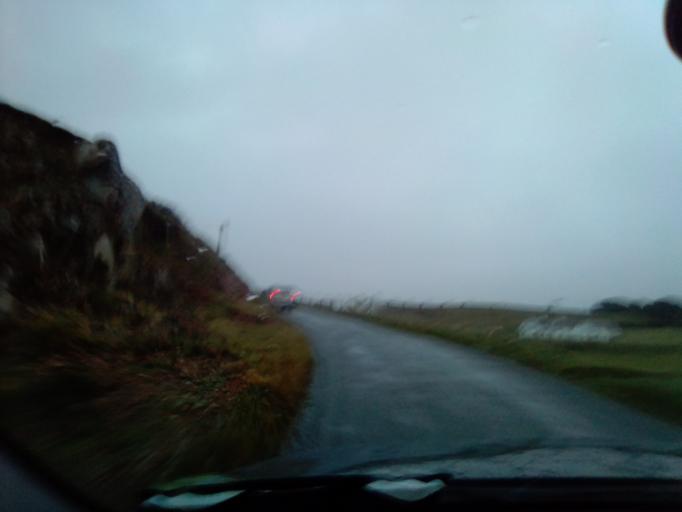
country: IE
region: Ulster
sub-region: County Donegal
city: Ramelton
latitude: 55.2542
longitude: -7.6778
